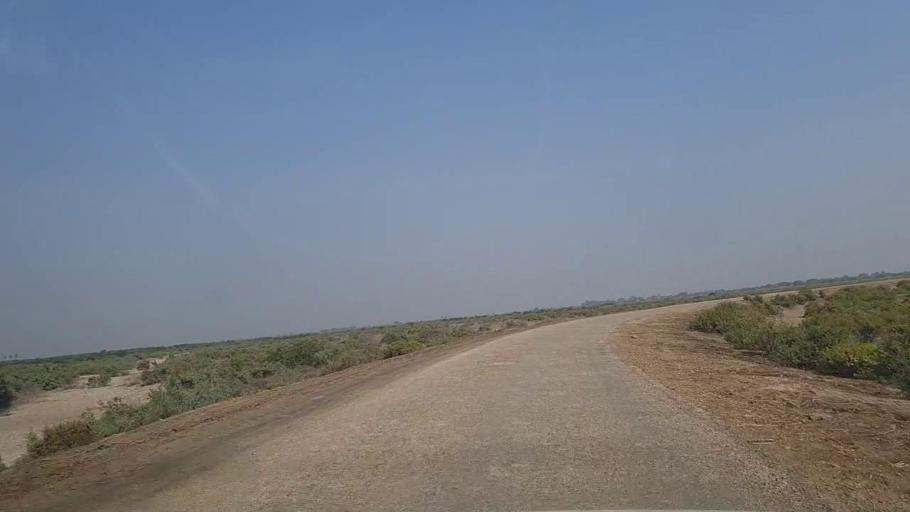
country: PK
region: Sindh
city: Keti Bandar
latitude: 24.2396
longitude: 67.6845
